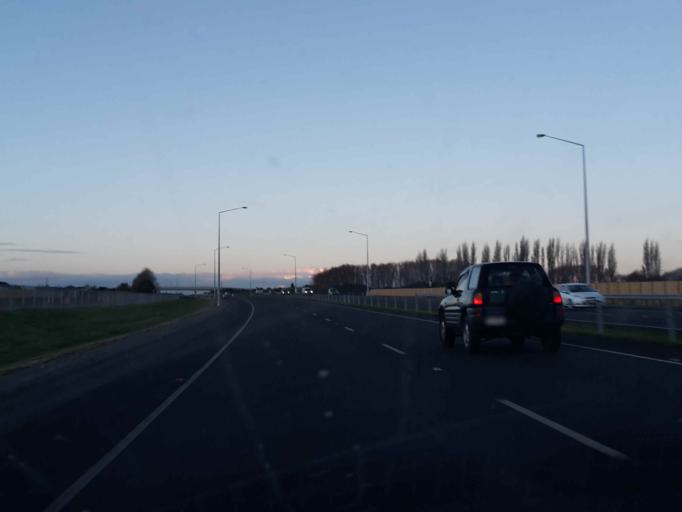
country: NZ
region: Canterbury
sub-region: Selwyn District
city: Prebbleton
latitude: -43.5627
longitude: 172.5580
